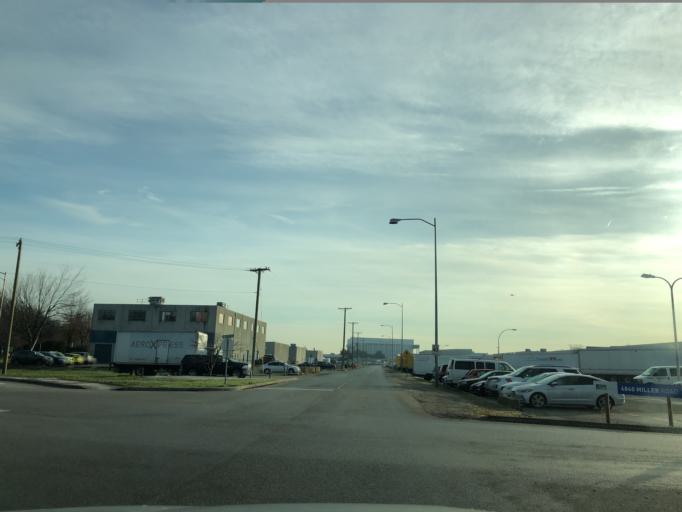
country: CA
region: British Columbia
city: Richmond
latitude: 49.1912
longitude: -123.1755
